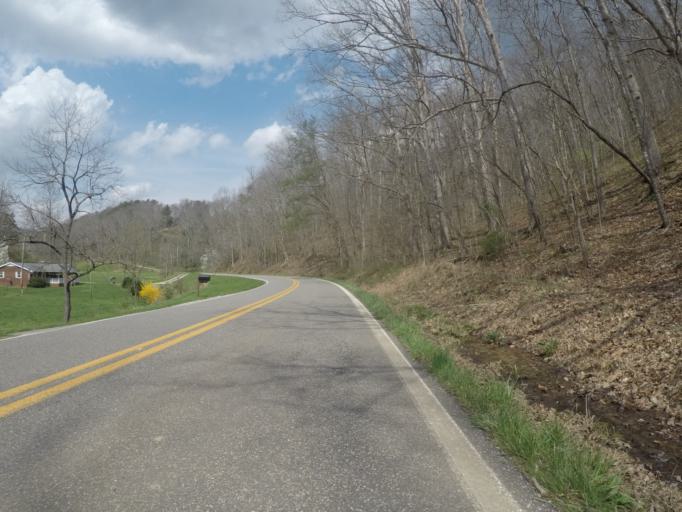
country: US
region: West Virginia
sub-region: Cabell County
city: Pea Ridge
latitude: 38.3412
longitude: -82.3403
